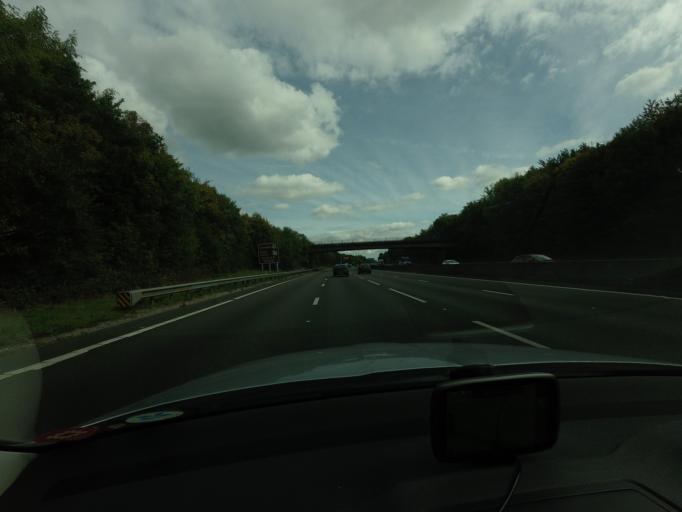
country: GB
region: England
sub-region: Kent
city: Westerham
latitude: 51.2852
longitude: 0.1095
